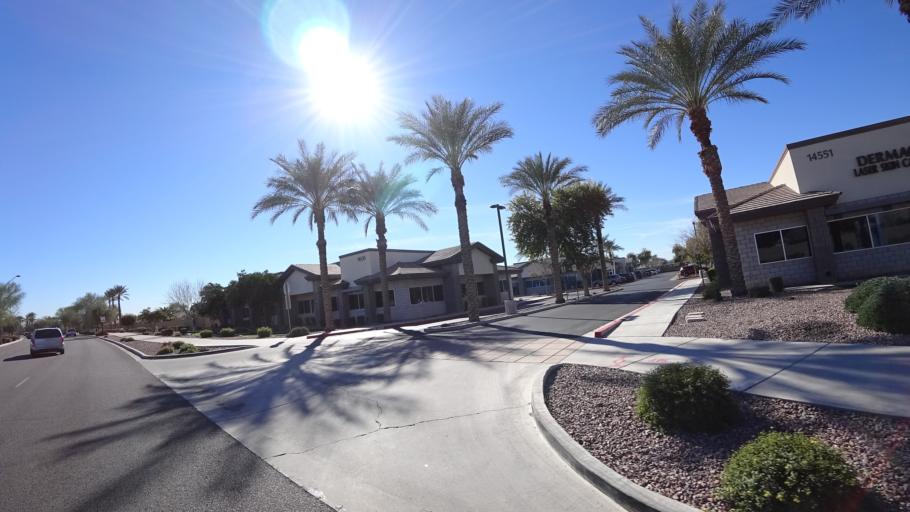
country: US
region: Arizona
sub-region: Maricopa County
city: Litchfield Park
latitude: 33.4864
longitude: -112.3727
